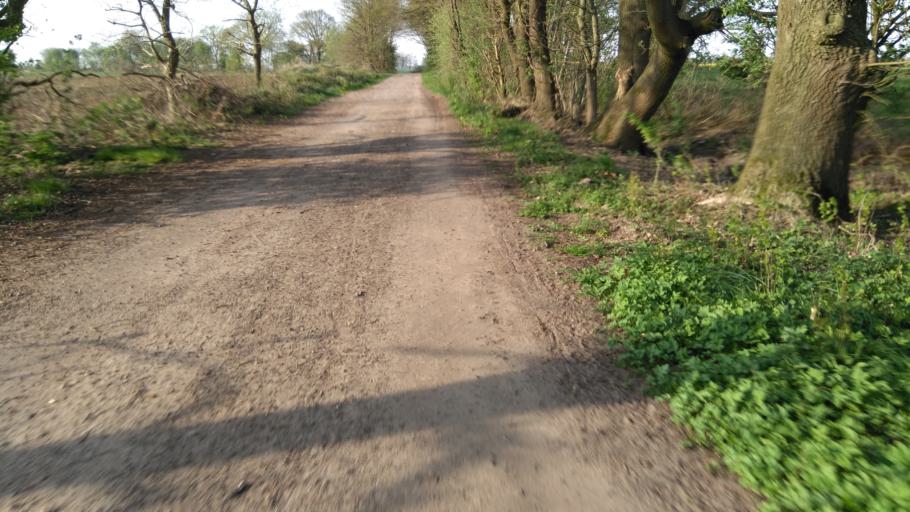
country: DE
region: Lower Saxony
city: Apensen
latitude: 53.4392
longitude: 9.6355
